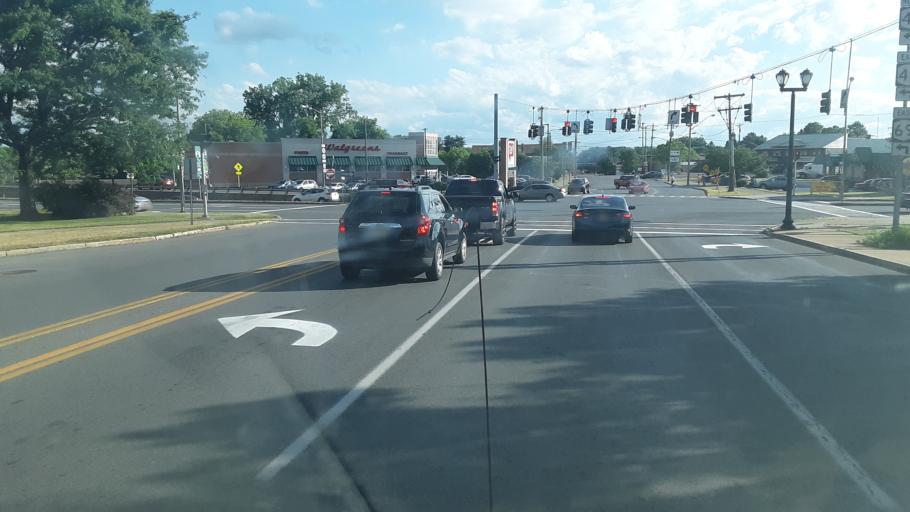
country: US
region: New York
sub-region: Oneida County
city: Rome
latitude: 43.2102
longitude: -75.4579
